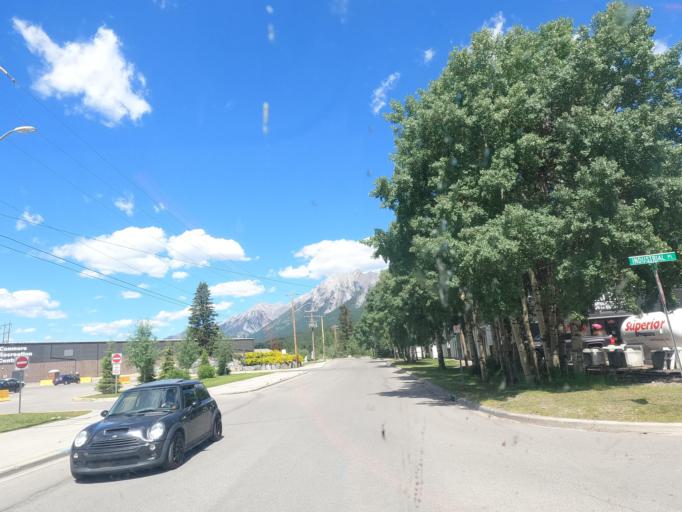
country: CA
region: Alberta
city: Canmore
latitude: 51.0991
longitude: -115.3632
